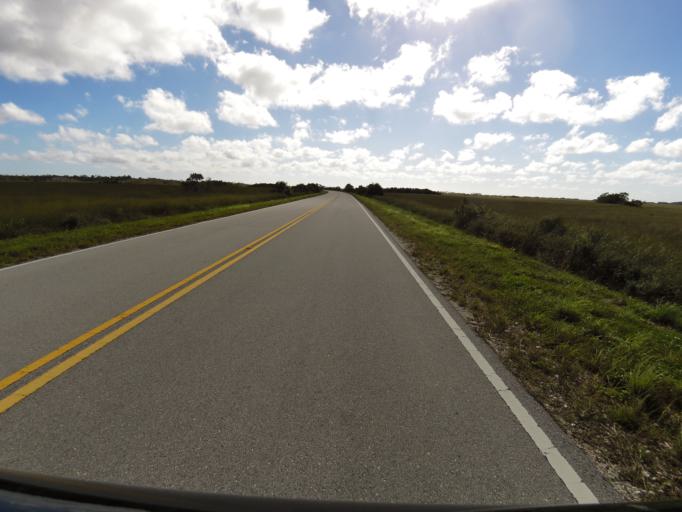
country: US
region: Florida
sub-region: Miami-Dade County
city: Florida City
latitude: 25.3602
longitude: -80.8209
